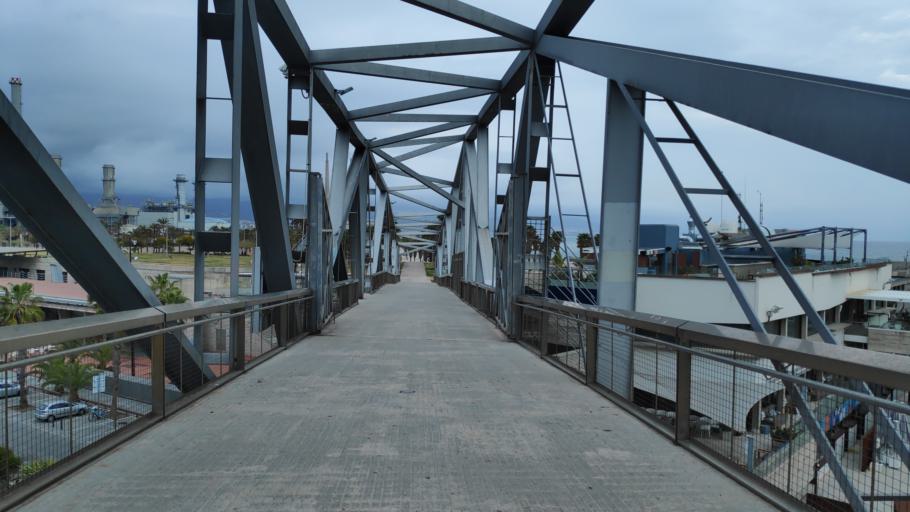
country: ES
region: Catalonia
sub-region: Provincia de Barcelona
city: Sant Adria de Besos
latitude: 41.4135
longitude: 2.2289
